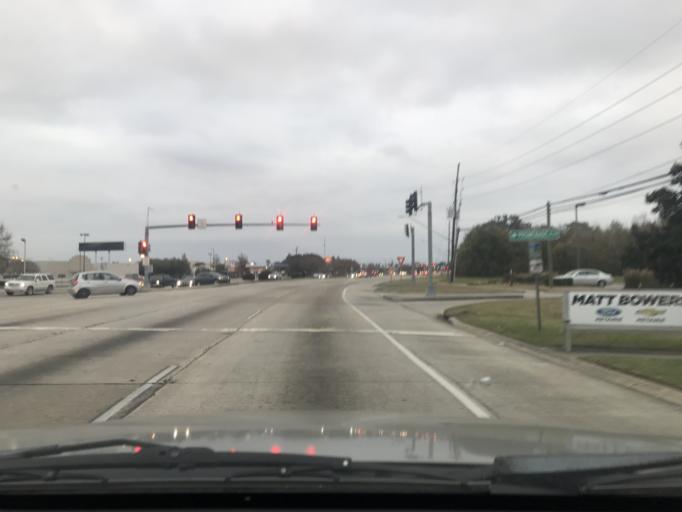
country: US
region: Louisiana
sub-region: Jefferson Parish
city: Woodmere
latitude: 29.8750
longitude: -90.0941
